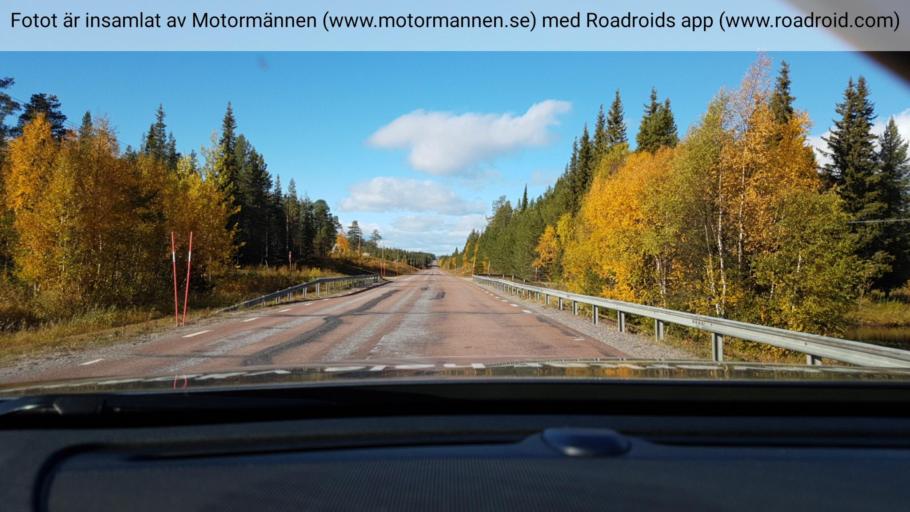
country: SE
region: Norrbotten
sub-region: Arjeplogs Kommun
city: Arjeplog
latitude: 66.0518
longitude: 18.0155
